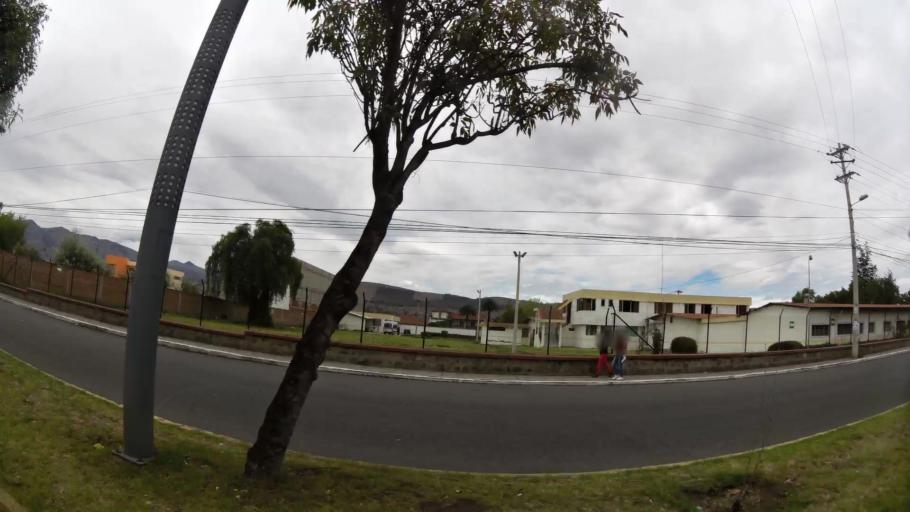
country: EC
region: Cotopaxi
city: San Miguel de Salcedo
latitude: -1.0389
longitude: -78.5907
